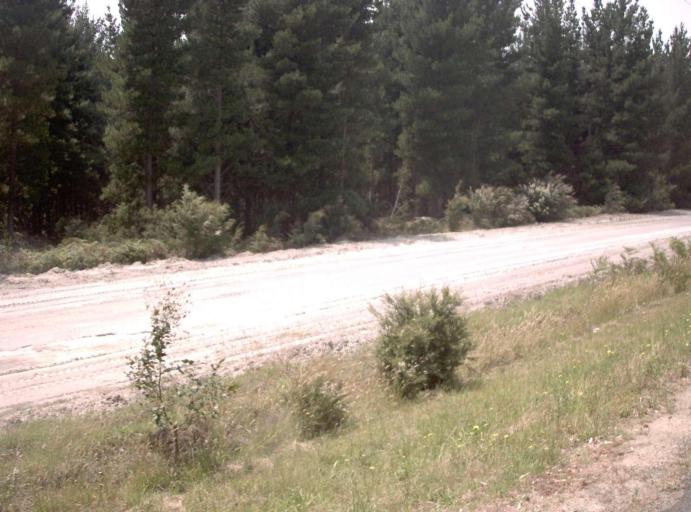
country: AU
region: Victoria
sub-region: Latrobe
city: Traralgon
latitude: -38.2624
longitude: 146.6820
